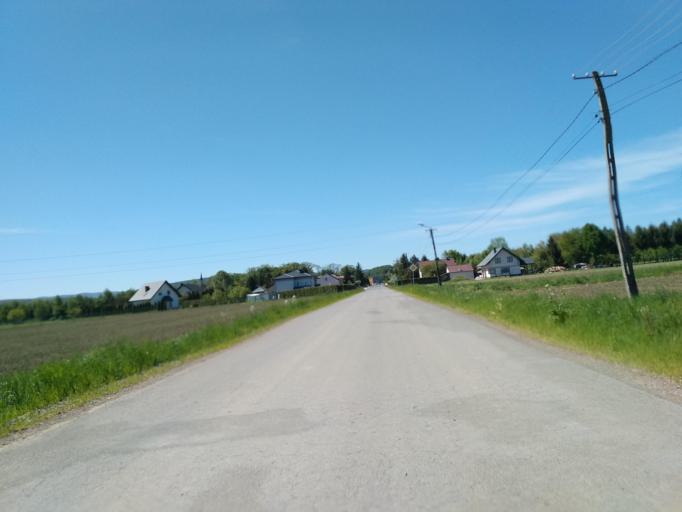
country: PL
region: Subcarpathian Voivodeship
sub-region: Powiat sanocki
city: Besko
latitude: 49.5982
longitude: 21.9684
